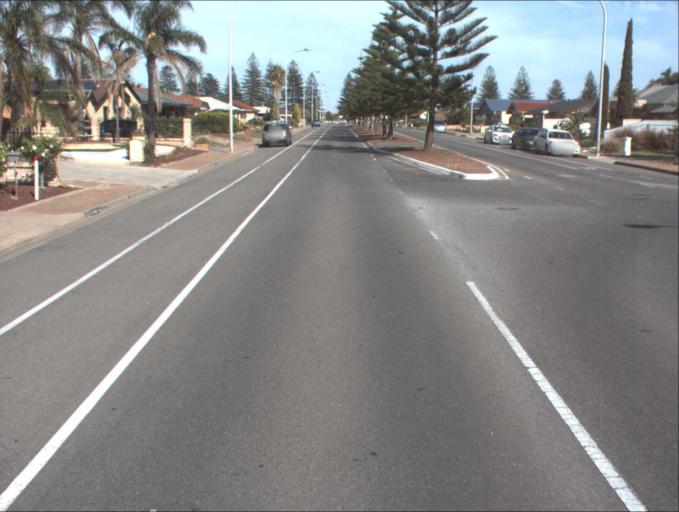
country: AU
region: South Australia
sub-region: Port Adelaide Enfield
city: Birkenhead
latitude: -34.7925
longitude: 138.4957
